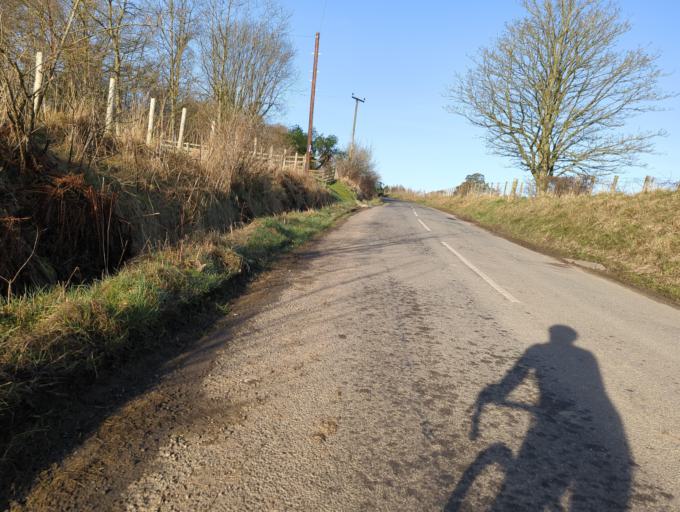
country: GB
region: Scotland
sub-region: Perth and Kinross
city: Methven
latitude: 56.4561
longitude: -3.5545
